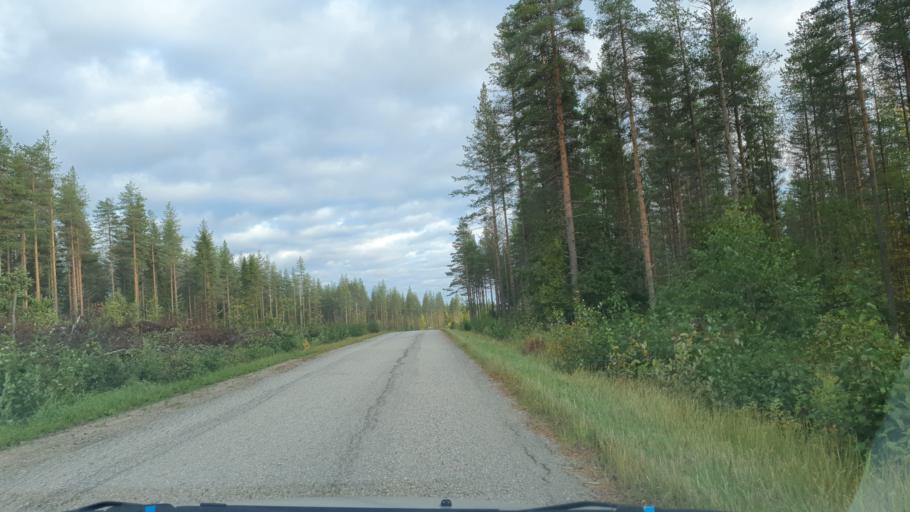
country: FI
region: North Karelia
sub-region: Pielisen Karjala
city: Lieksa
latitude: 63.9212
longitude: 30.1541
